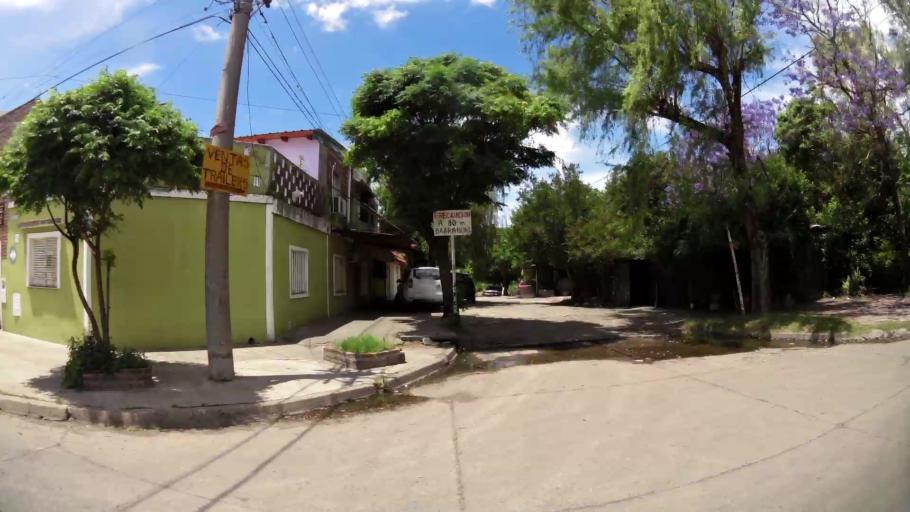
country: AR
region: Santa Fe
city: Gobernador Galvez
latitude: -33.0020
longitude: -60.6206
